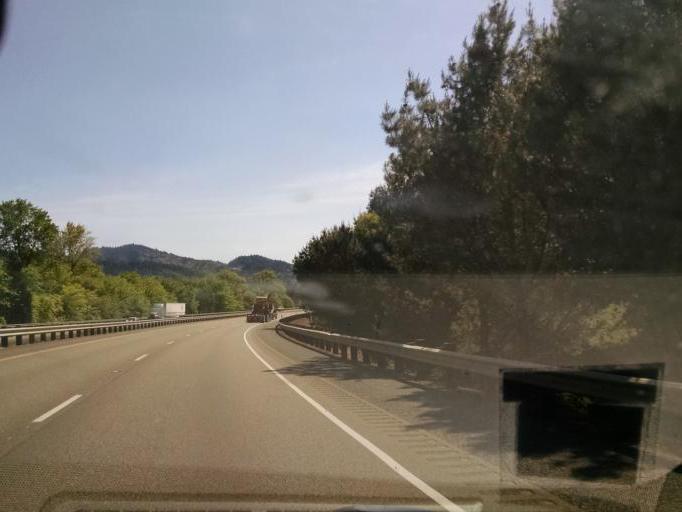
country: US
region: Oregon
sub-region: Douglas County
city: Myrtle Creek
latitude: 43.0134
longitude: -123.3006
